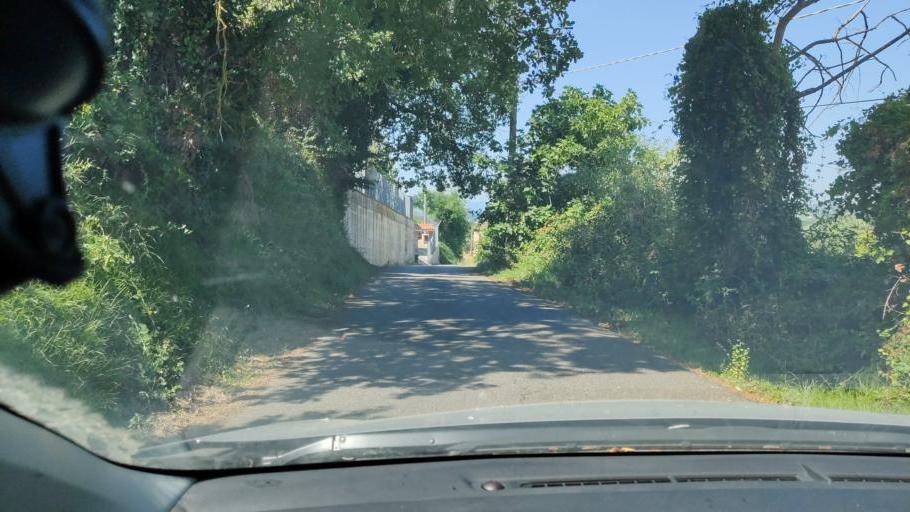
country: IT
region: Umbria
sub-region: Provincia di Terni
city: Fornole
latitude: 42.5401
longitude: 12.4520
